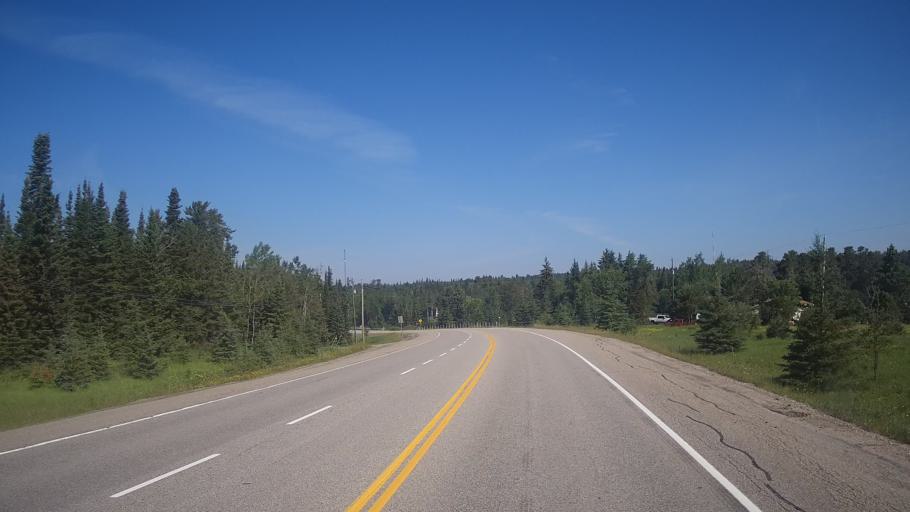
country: CA
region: Ontario
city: Dryden
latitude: 49.7168
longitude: -92.5958
